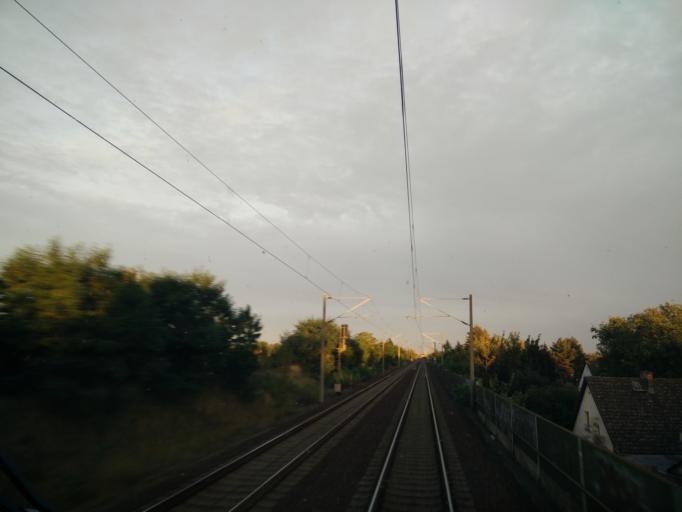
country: DE
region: Berlin
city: Staaken
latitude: 52.5479
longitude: 13.1349
